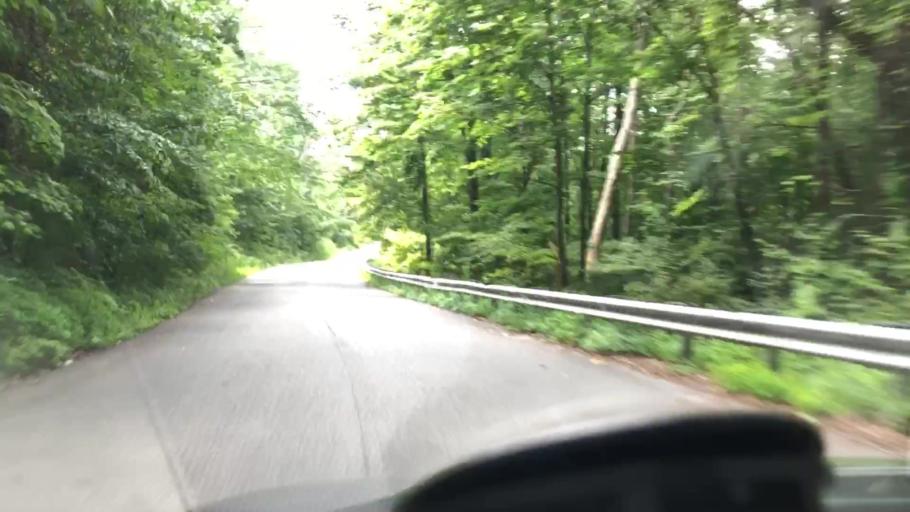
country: US
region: Massachusetts
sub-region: Berkshire County
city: North Adams
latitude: 42.6851
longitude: -73.1461
